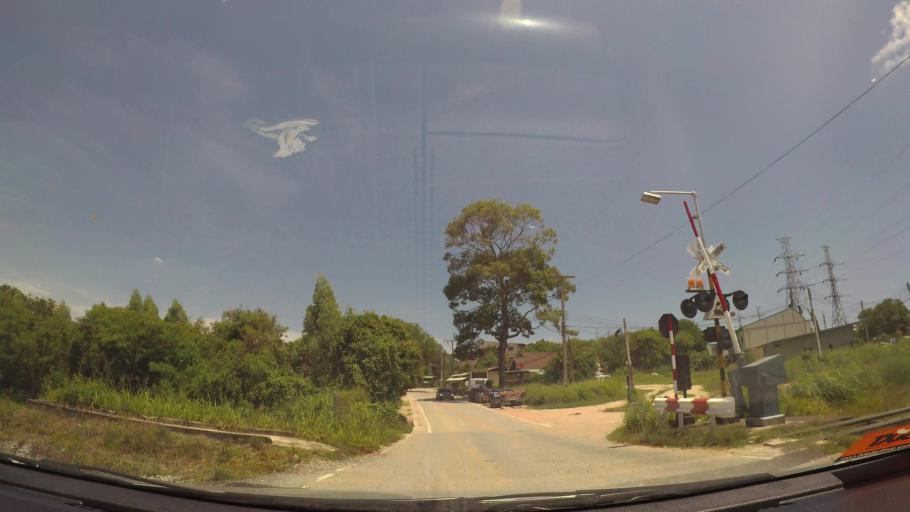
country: TH
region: Chon Buri
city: Si Racha
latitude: 13.1326
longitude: 100.9447
